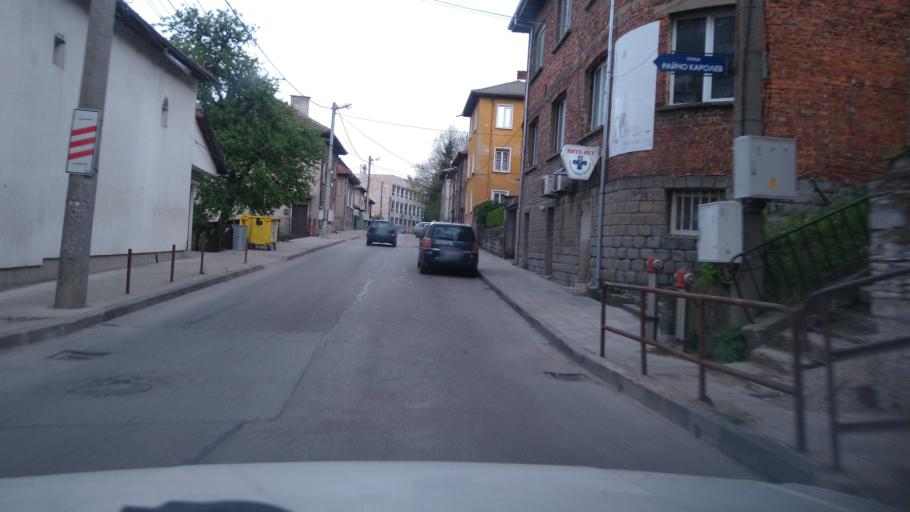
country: BG
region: Gabrovo
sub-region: Obshtina Gabrovo
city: Gabrovo
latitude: 42.8676
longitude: 25.3155
